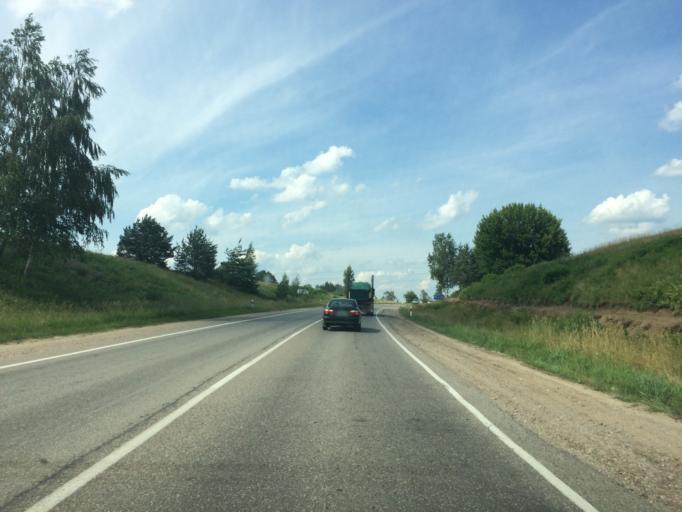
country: LT
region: Kauno apskritis
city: Jonava
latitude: 55.0912
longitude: 24.3126
